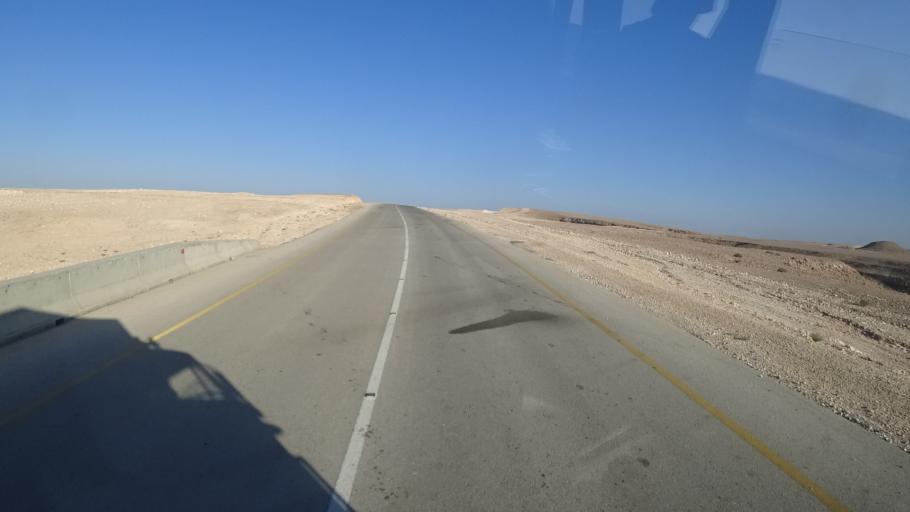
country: YE
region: Al Mahrah
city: Hawf
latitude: 17.0870
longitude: 53.0756
